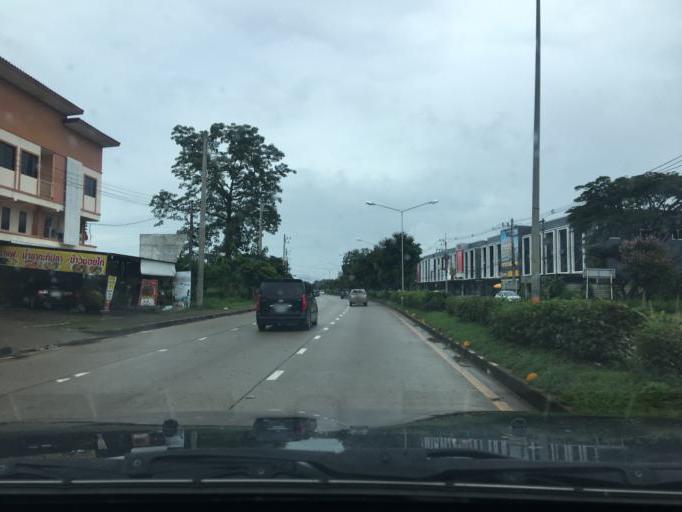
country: TH
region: Chiang Rai
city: Chiang Rai
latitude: 19.9206
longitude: 99.8614
